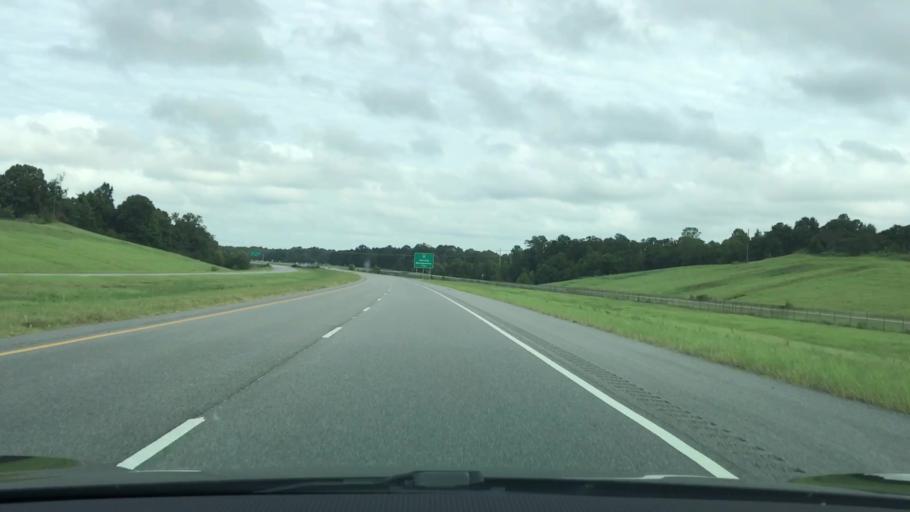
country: US
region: Alabama
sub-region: Montgomery County
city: Pike Road
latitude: 32.3505
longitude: -86.0657
